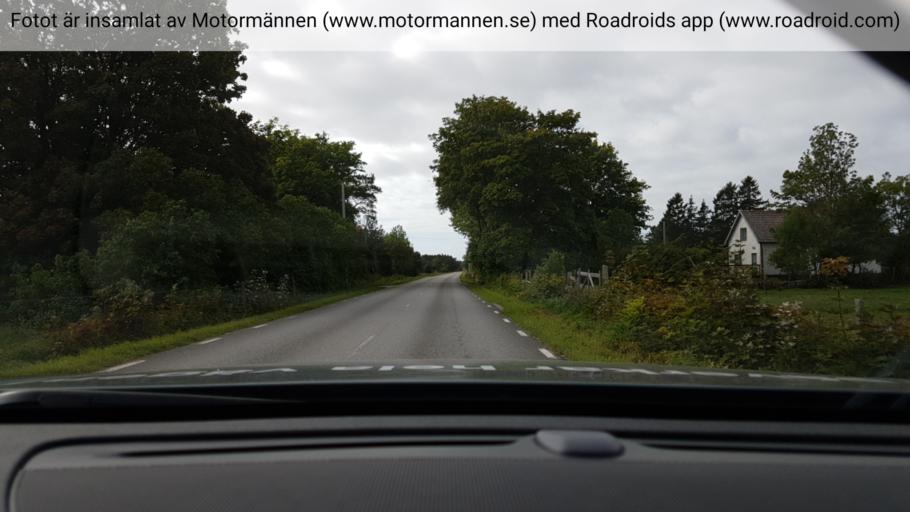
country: SE
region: Gotland
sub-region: Gotland
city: Hemse
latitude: 56.9629
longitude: 18.2241
